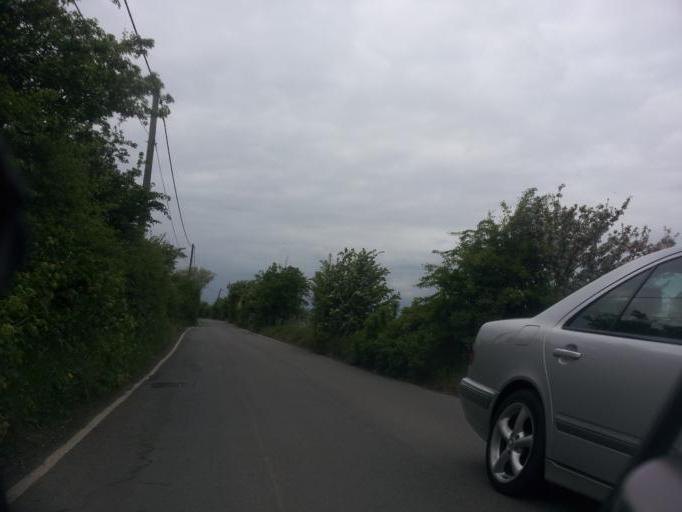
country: GB
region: England
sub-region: Kent
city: Queenborough
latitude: 51.3860
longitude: 0.7299
